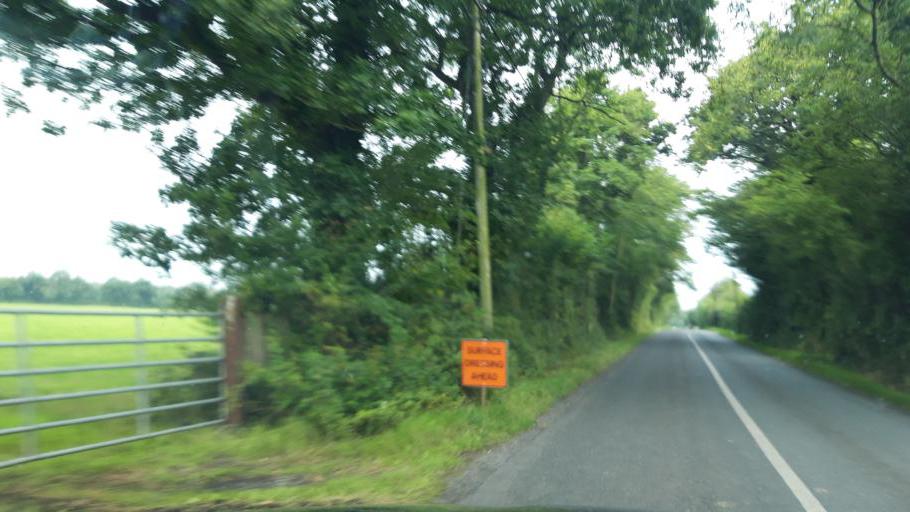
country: IE
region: Leinster
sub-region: Kilkenny
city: Callan
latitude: 52.5196
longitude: -7.5104
